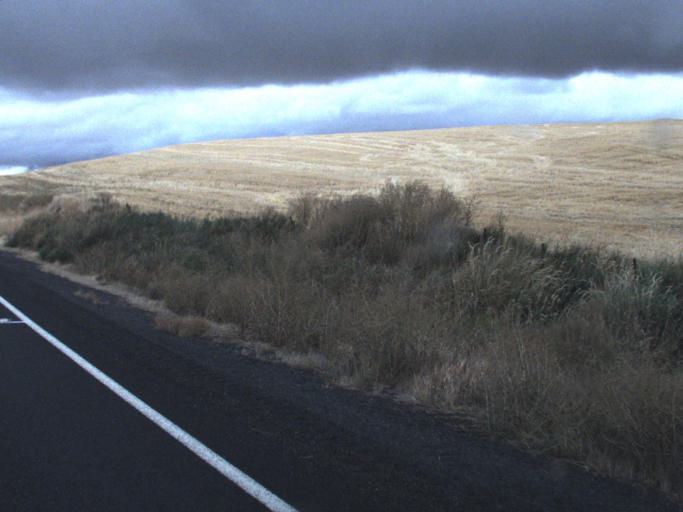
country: US
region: Washington
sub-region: Whitman County
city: Colfax
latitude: 47.1397
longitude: -117.2474
